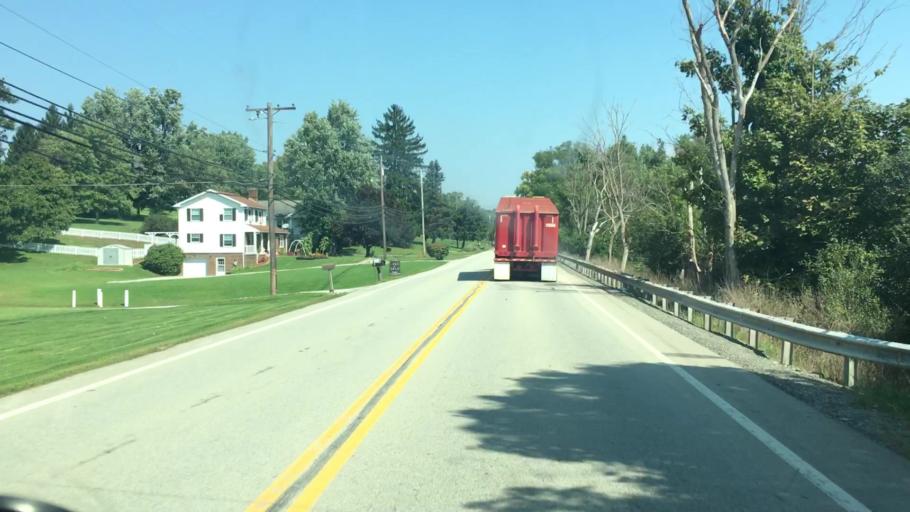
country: US
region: Pennsylvania
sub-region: Washington County
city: Washington
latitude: 40.1376
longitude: -80.2740
